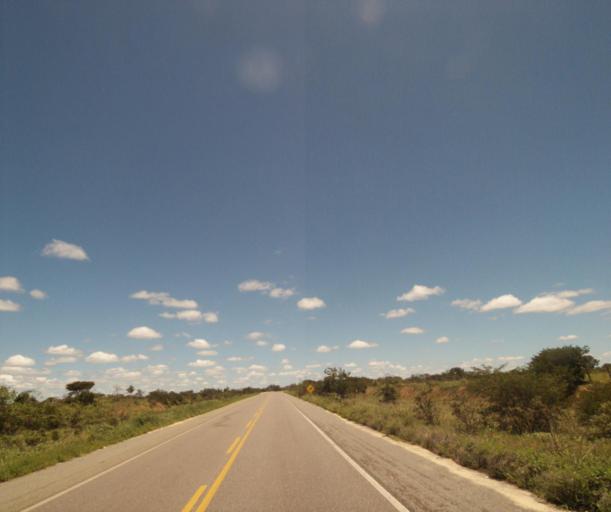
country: BR
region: Bahia
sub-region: Carinhanha
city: Carinhanha
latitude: -14.2933
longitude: -43.7856
